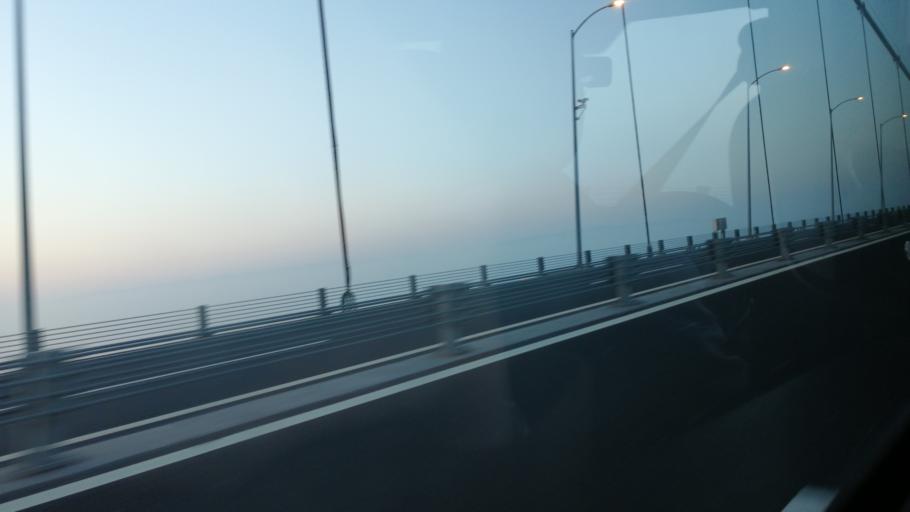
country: TR
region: Yalova
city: Altinova
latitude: 40.7511
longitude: 29.5153
